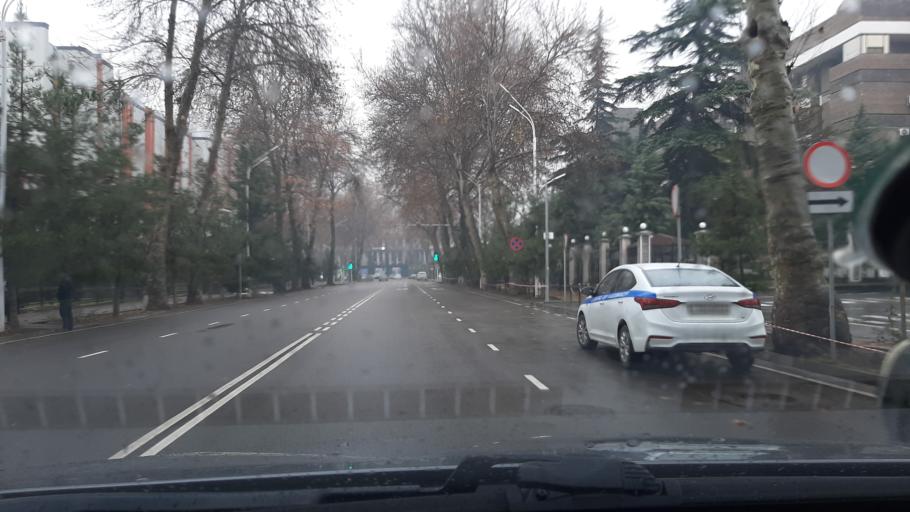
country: TJ
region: Dushanbe
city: Dushanbe
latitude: 38.5714
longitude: 68.7844
